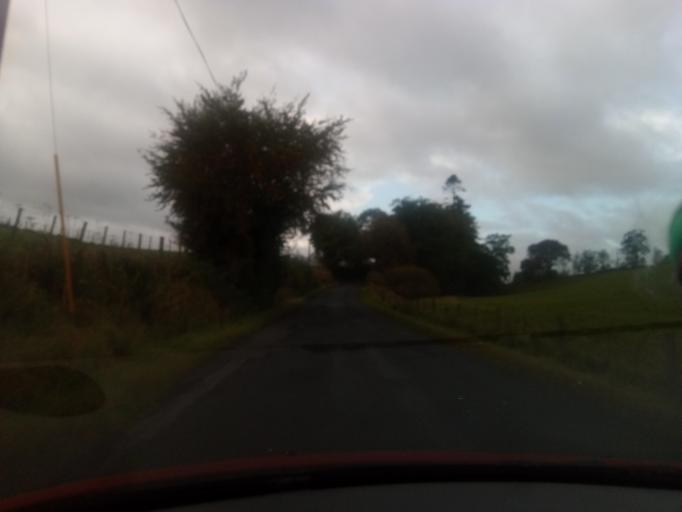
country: GB
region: Scotland
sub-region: The Scottish Borders
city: Jedburgh
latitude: 55.4513
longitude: -2.5680
